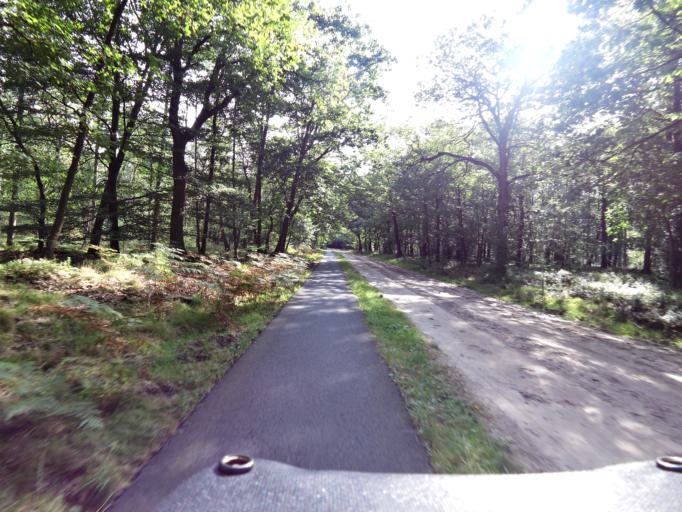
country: NL
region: Gelderland
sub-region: Gemeente Apeldoorn
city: Uddel
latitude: 52.2134
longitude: 5.8024
